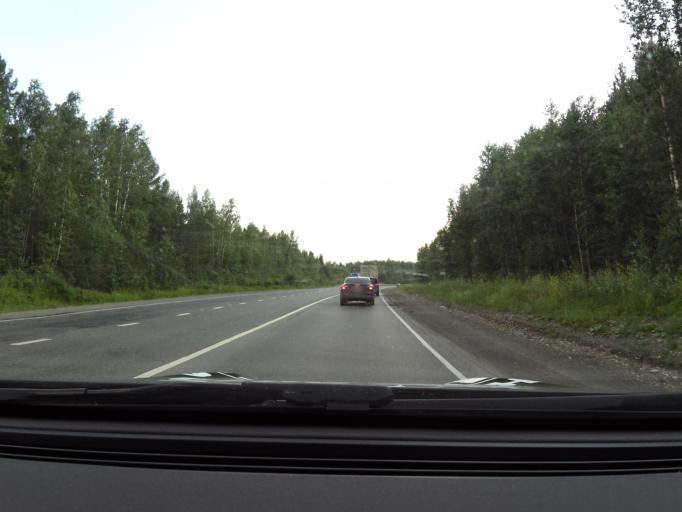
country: RU
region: Sverdlovsk
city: Talitsa
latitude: 56.8291
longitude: 59.9931
